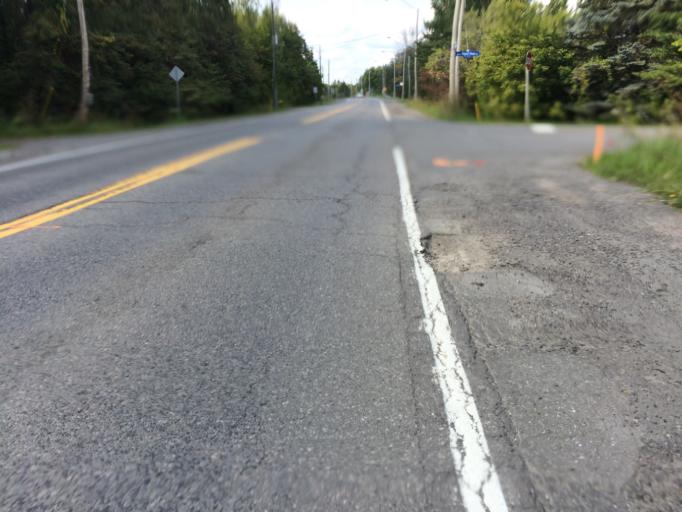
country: CA
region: Ontario
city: Bells Corners
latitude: 45.2173
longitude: -75.6713
